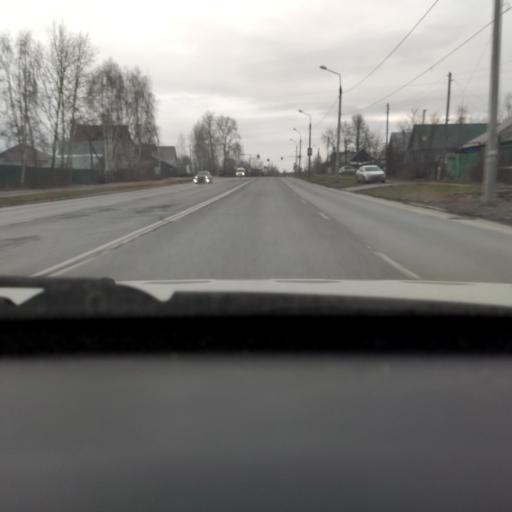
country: RU
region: Perm
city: Polazna
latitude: 58.1214
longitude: 56.4036
